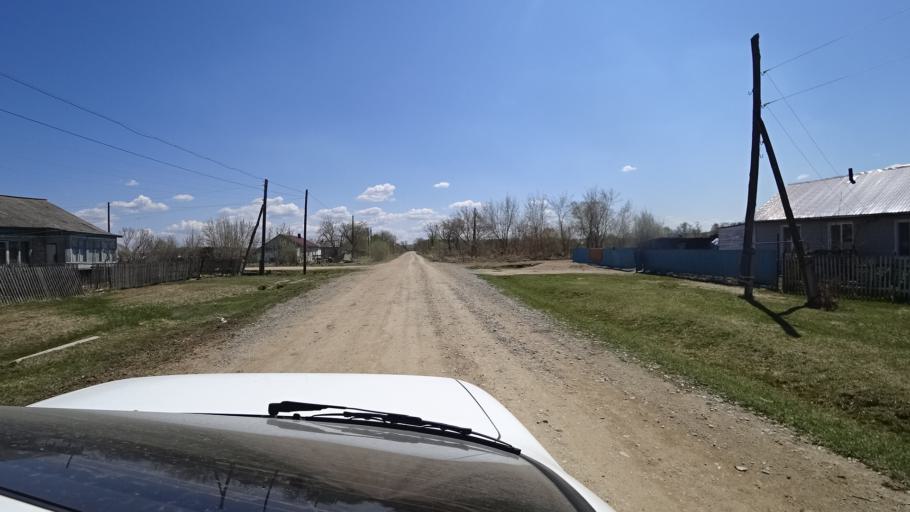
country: RU
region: Primorskiy
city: Dal'nerechensk
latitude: 45.8015
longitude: 133.7653
